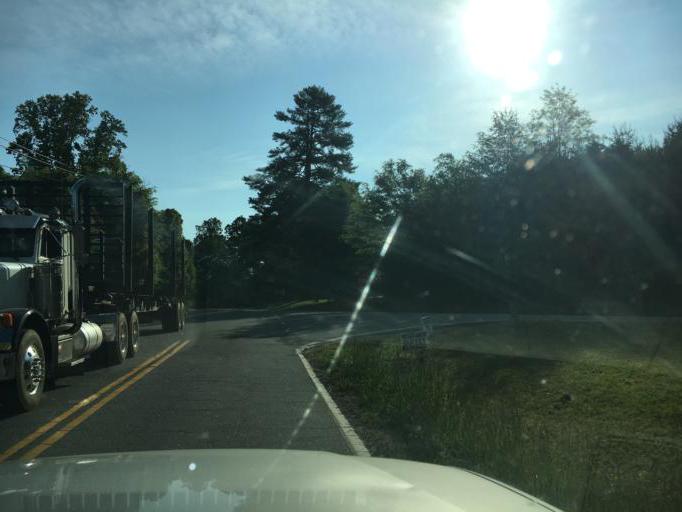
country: US
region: North Carolina
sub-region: Rutherford County
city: Rutherfordton
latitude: 35.3781
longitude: -81.9643
